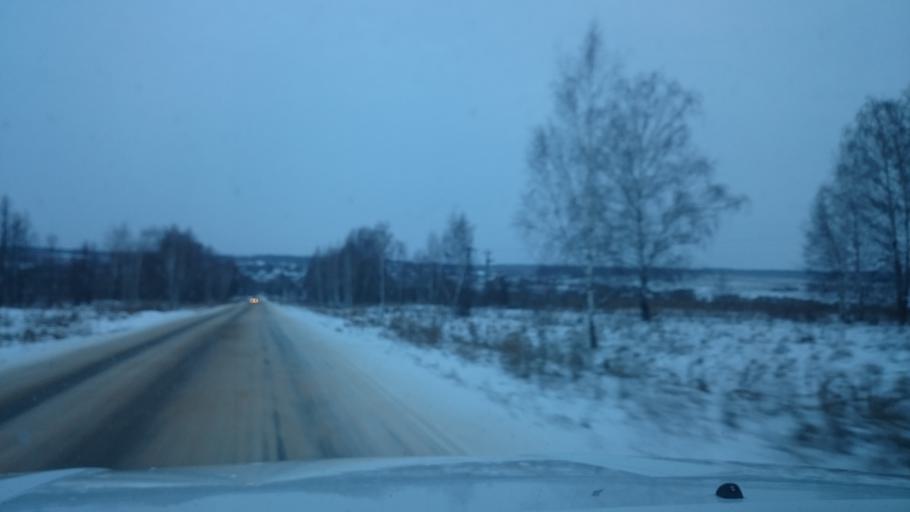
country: RU
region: Tula
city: Leninskiy
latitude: 54.2433
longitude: 37.2769
